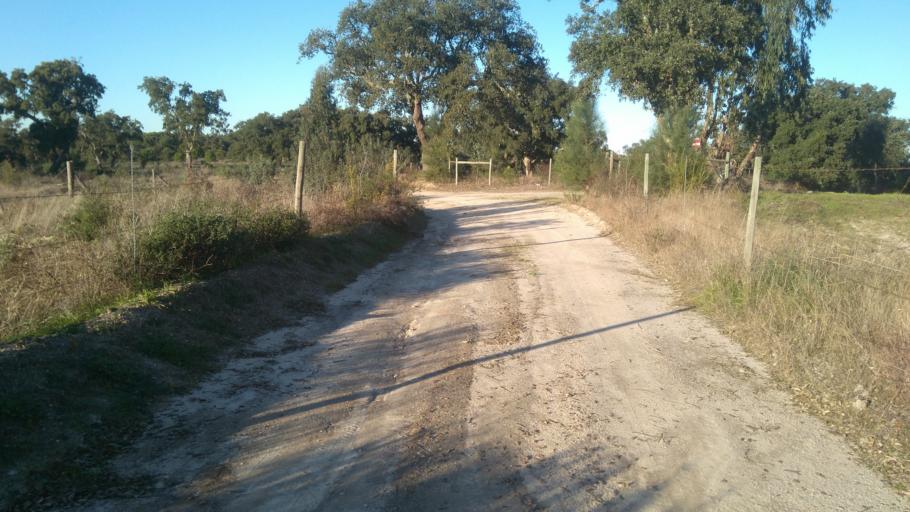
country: PT
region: Santarem
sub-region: Coruche
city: Coruche
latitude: 38.8614
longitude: -8.5258
